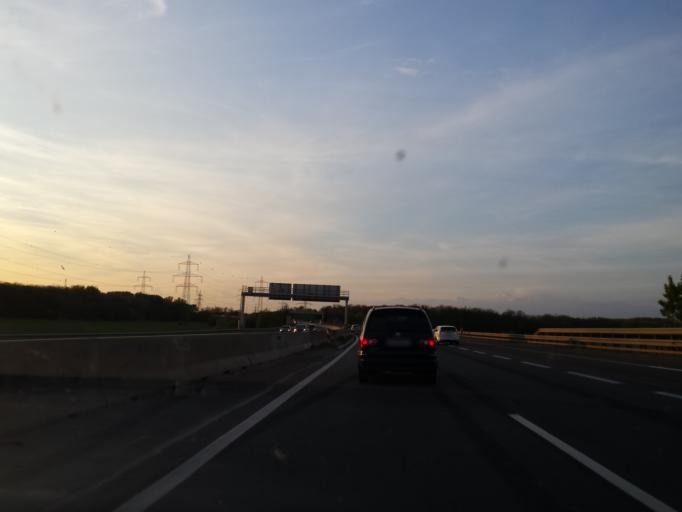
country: AT
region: Burgenland
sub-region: Politischer Bezirk Neusiedl am See
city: Parndorf
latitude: 48.0239
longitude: 16.8365
